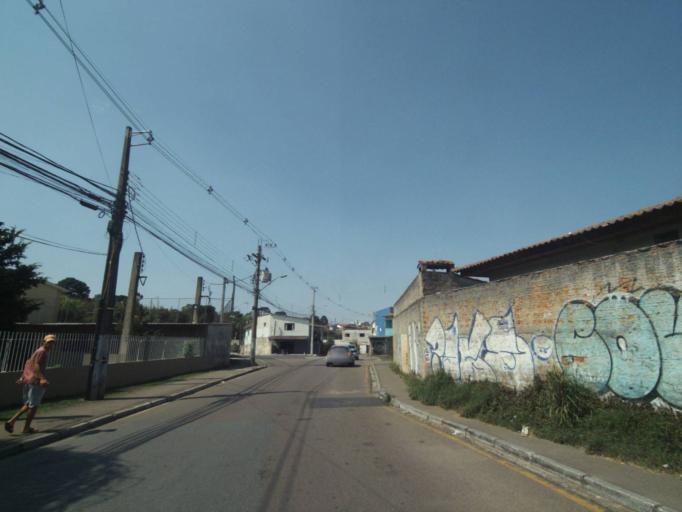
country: BR
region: Parana
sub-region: Curitiba
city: Curitiba
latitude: -25.4788
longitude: -49.3212
